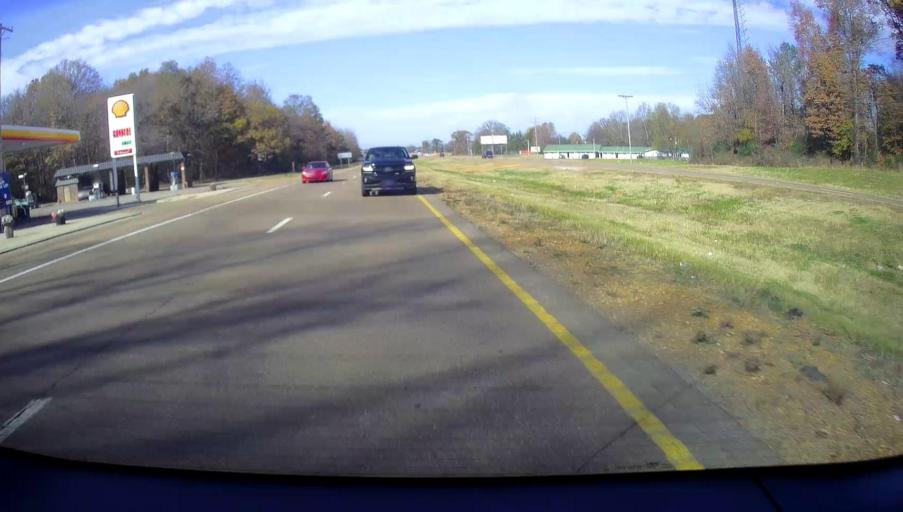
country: US
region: Tennessee
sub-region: Fayette County
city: Piperton
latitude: 34.9912
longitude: -89.6133
